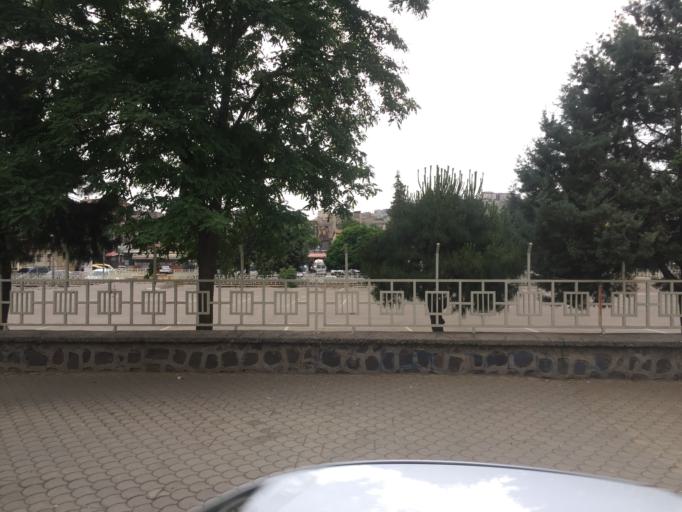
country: TR
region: Gaziantep
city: Gaziantep
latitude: 37.0678
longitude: 37.4141
